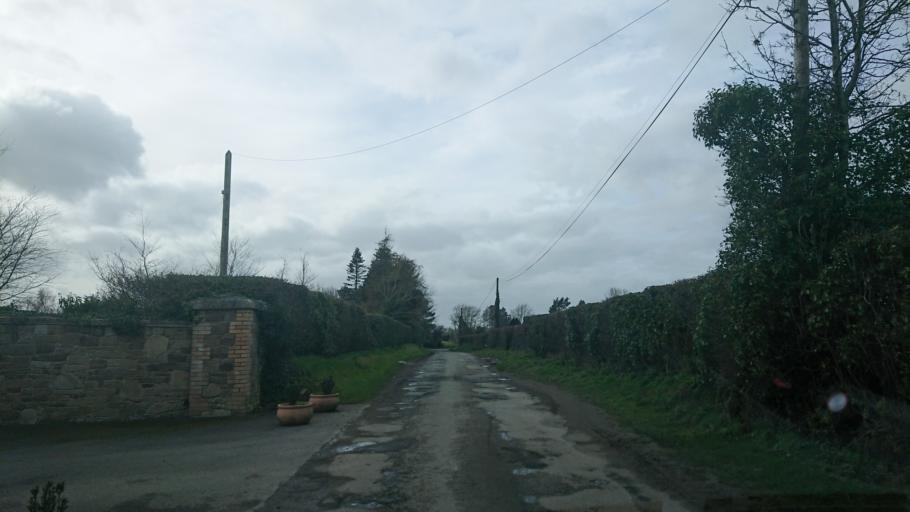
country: IE
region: Leinster
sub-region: Kildare
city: Naas
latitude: 53.1733
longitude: -6.6286
